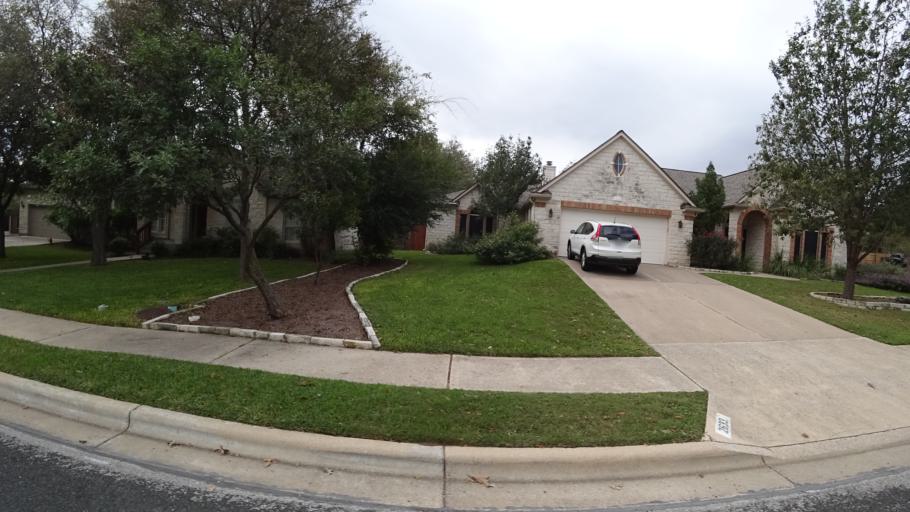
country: US
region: Texas
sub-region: Travis County
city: Shady Hollow
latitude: 30.1568
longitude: -97.8488
